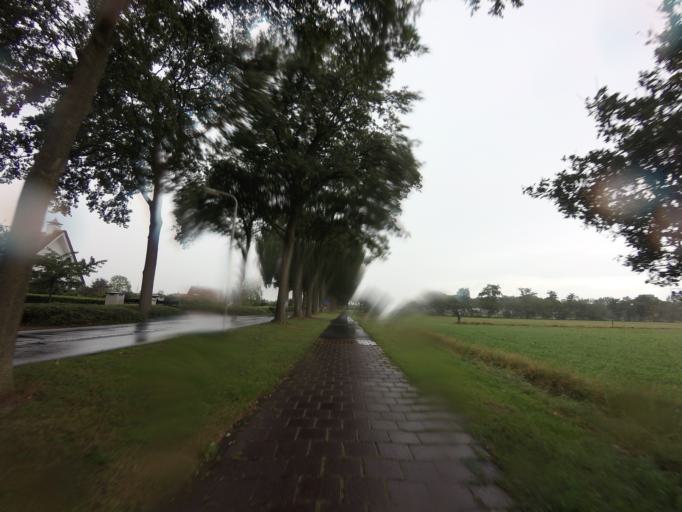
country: NL
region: Drenthe
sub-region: Gemeente Hoogeveen
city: Hoogeveen
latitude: 52.6682
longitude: 6.4960
